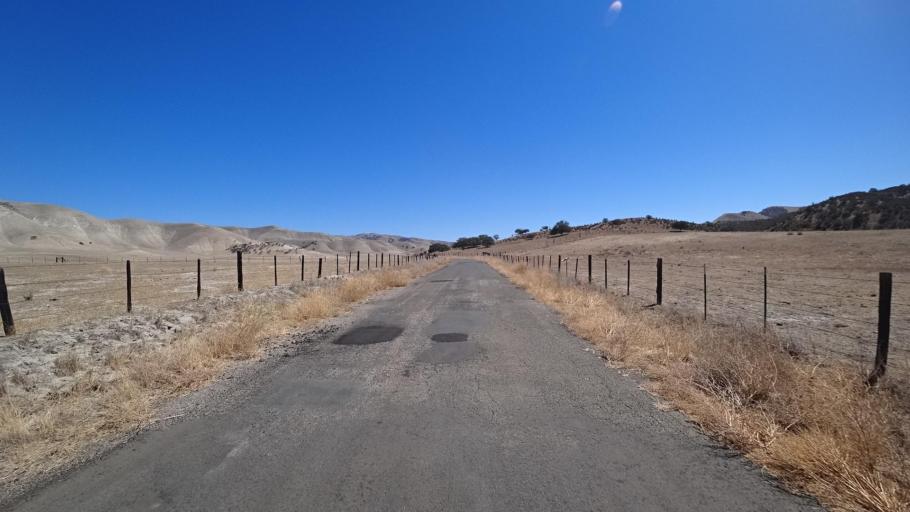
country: US
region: California
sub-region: Monterey County
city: King City
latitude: 36.2936
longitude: -120.9802
